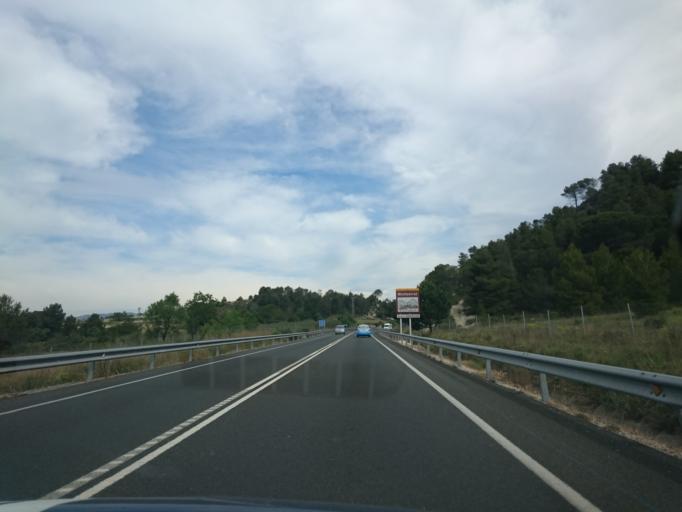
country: ES
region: Catalonia
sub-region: Provincia de Barcelona
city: La Pobla de Claramunt
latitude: 41.5707
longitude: 1.6742
